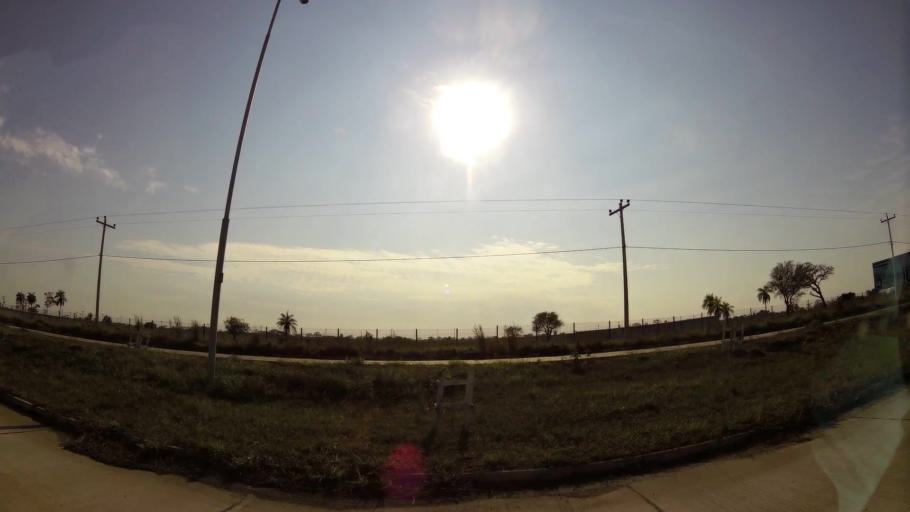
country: BO
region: Santa Cruz
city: Santa Cruz de la Sierra
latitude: -17.6811
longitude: -63.1207
